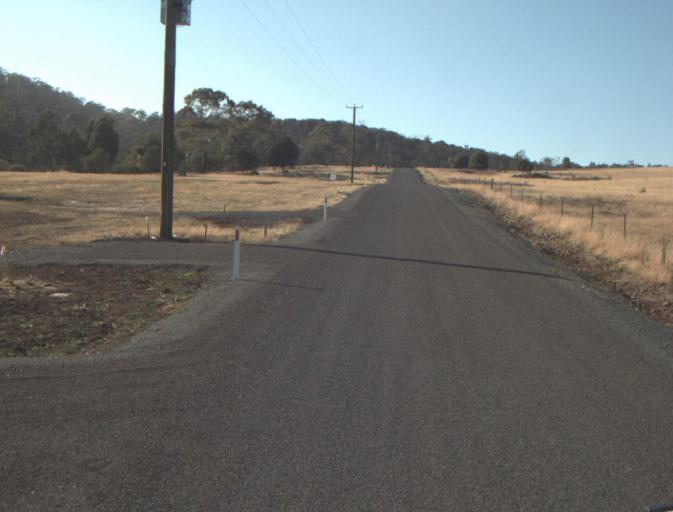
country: AU
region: Tasmania
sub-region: Launceston
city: Newstead
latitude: -41.4342
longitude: 147.2144
